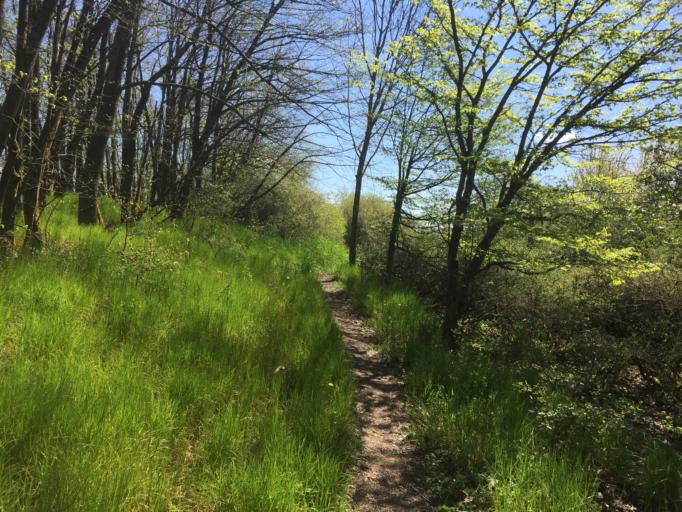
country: DE
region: Bavaria
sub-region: Regierungsbezirk Unterfranken
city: Sulzfeld
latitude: 50.2727
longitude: 10.4215
